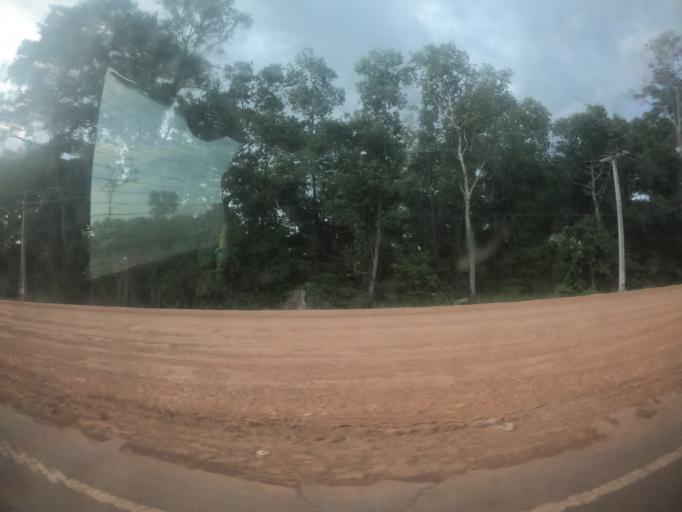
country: TH
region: Surin
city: Kap Choeng
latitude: 14.4623
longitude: 103.6520
